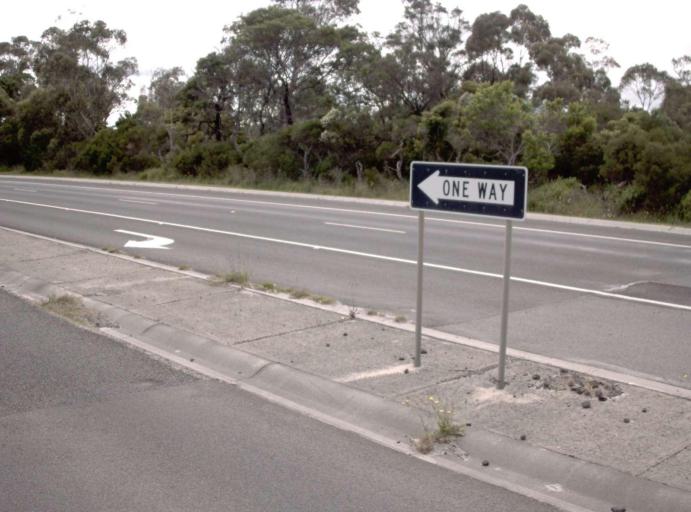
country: AU
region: Victoria
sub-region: Bass Coast
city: North Wonthaggi
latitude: -38.4120
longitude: 145.5271
